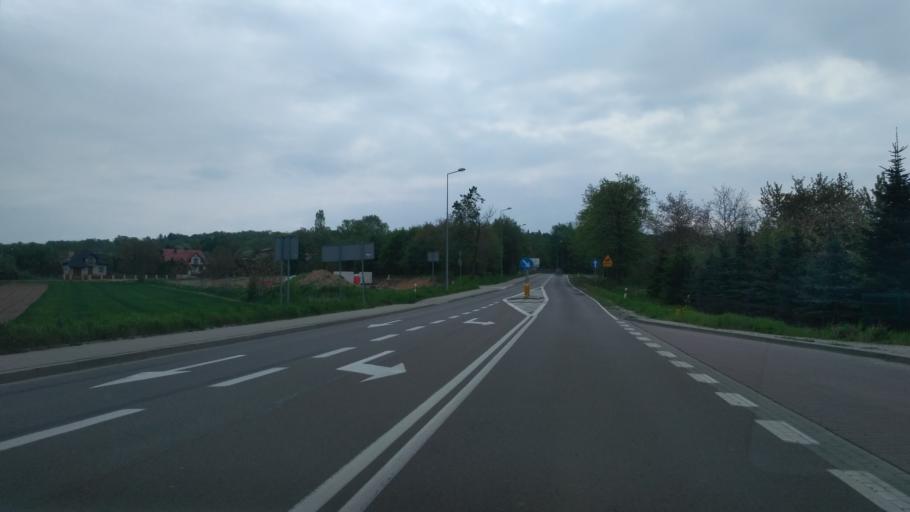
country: PL
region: Lesser Poland Voivodeship
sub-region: Powiat tarnowski
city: Tarnowiec
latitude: 49.9710
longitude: 20.9922
